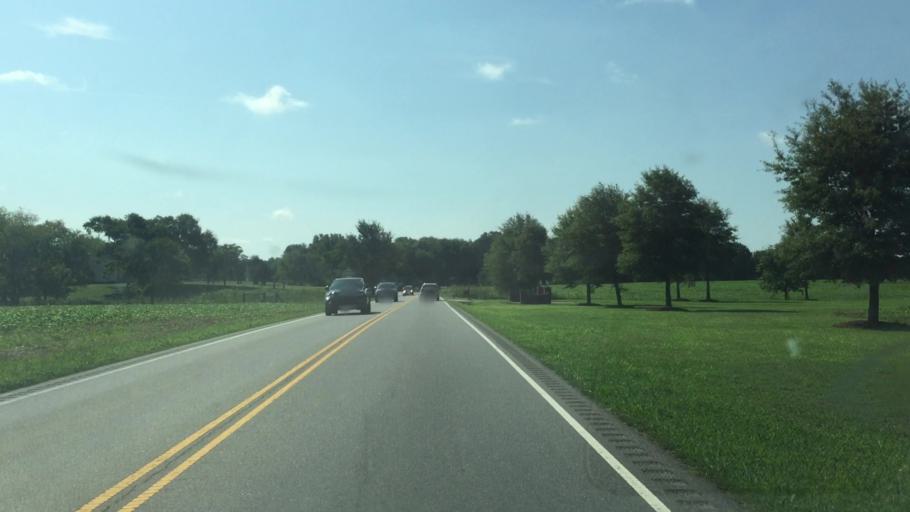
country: US
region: North Carolina
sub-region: Union County
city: Fairview
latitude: 35.1411
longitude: -80.5457
